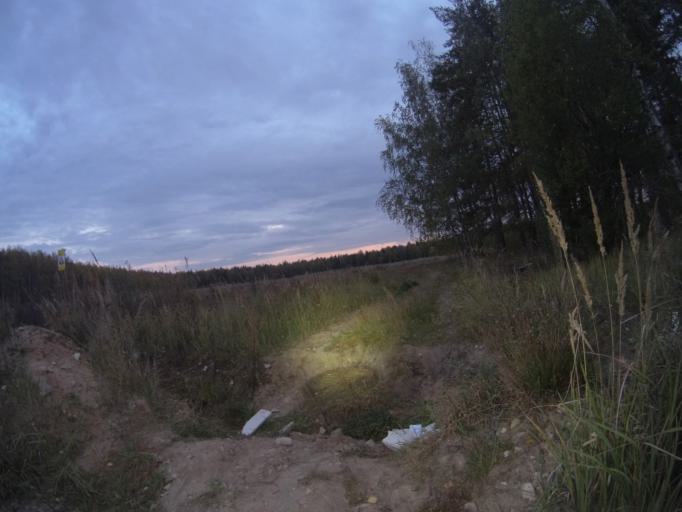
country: RU
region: Vladimir
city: Raduzhnyy
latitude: 55.9875
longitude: 40.2255
